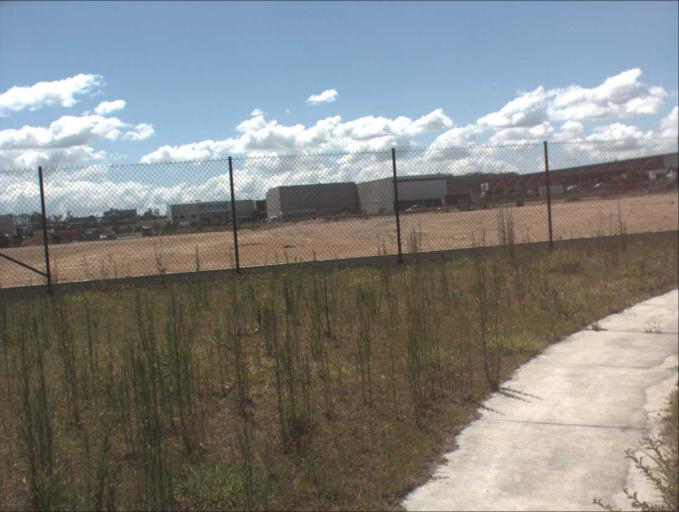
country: AU
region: Queensland
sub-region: Logan
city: Woodridge
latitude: -27.6481
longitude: 153.0906
